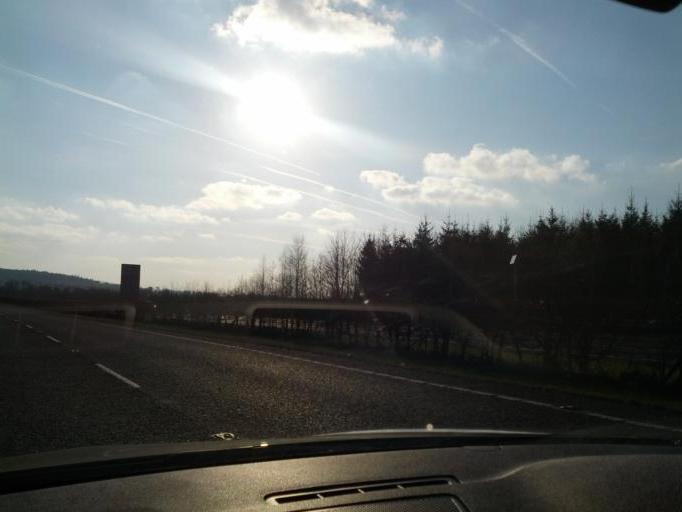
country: IE
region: Leinster
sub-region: Kildare
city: Monasterevin
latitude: 53.1415
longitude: -7.0279
